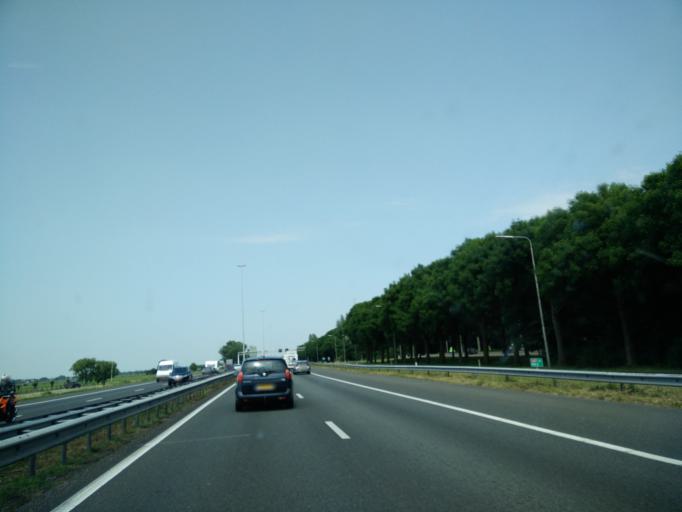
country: NL
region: Utrecht
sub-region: Gemeente Lopik
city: Lopik
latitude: 51.9114
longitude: 4.9841
